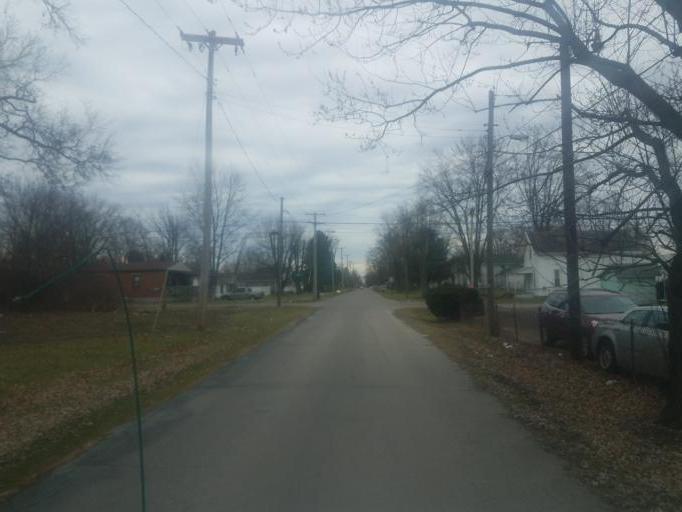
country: US
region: Ohio
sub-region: Marion County
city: Marion
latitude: 40.6080
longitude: -83.1286
